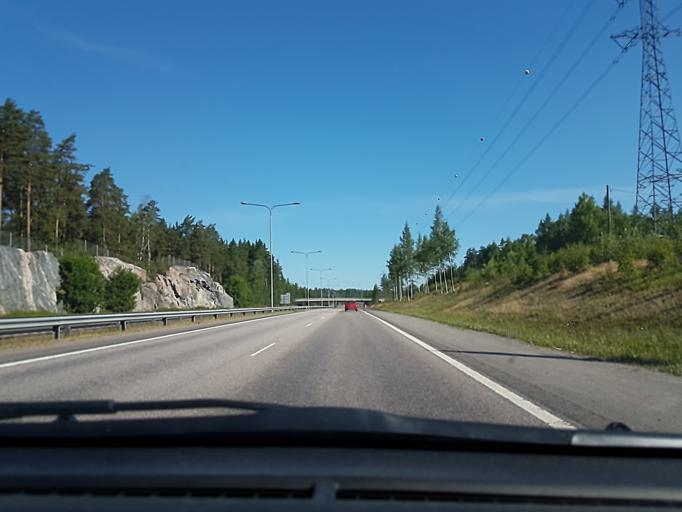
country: FI
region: Uusimaa
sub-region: Helsinki
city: Vantaa
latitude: 60.3144
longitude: 24.9978
